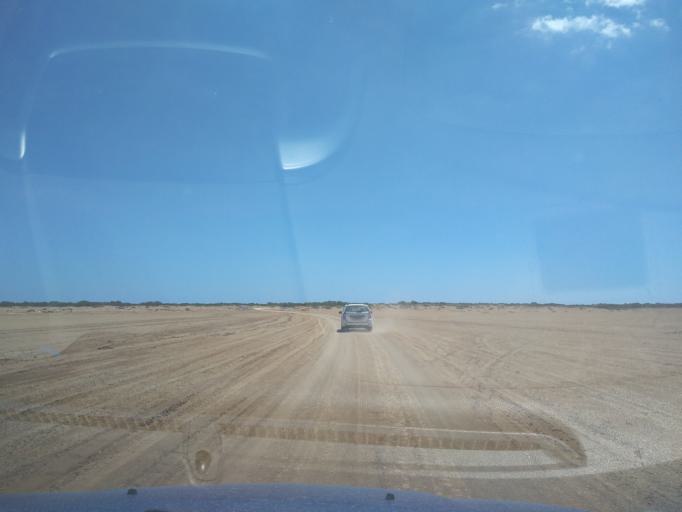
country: TN
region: Susah
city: Harqalah
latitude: 36.1623
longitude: 10.4569
